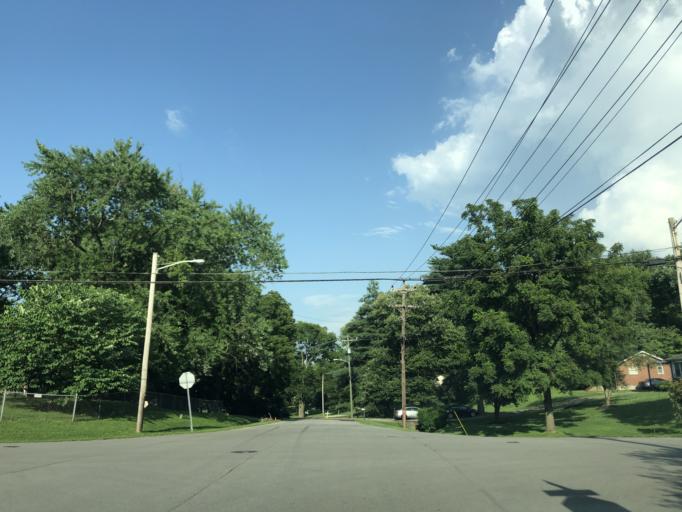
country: US
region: Tennessee
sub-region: Davidson County
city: Lakewood
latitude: 36.1521
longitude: -86.6586
